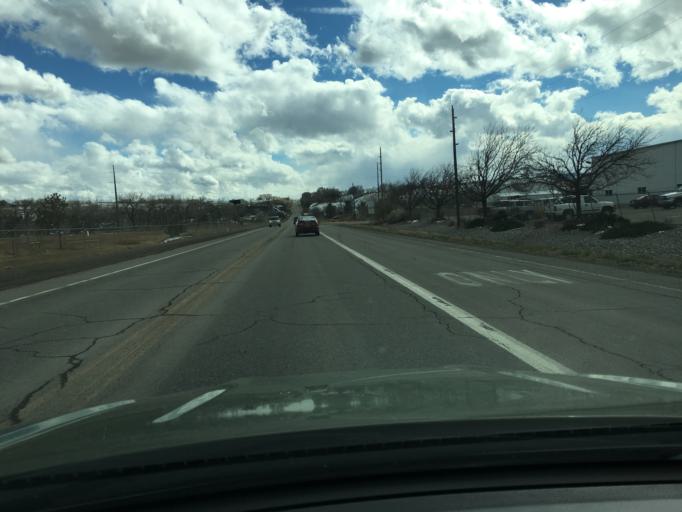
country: US
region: Colorado
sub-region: Mesa County
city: Clifton
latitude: 39.0602
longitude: -108.4595
